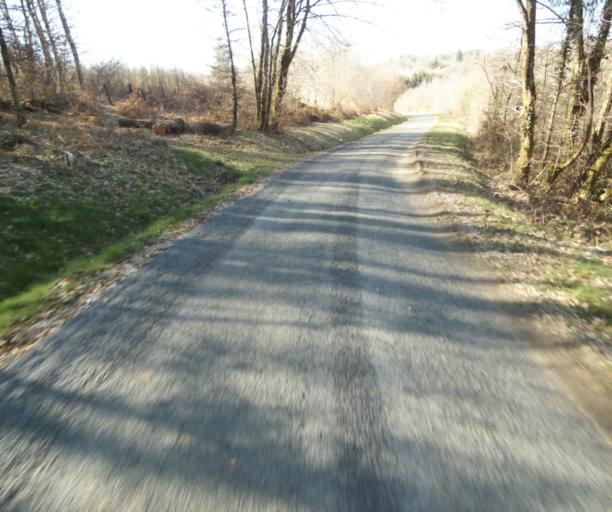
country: FR
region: Limousin
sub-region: Departement de la Correze
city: Chamboulive
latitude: 45.4180
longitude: 1.6460
